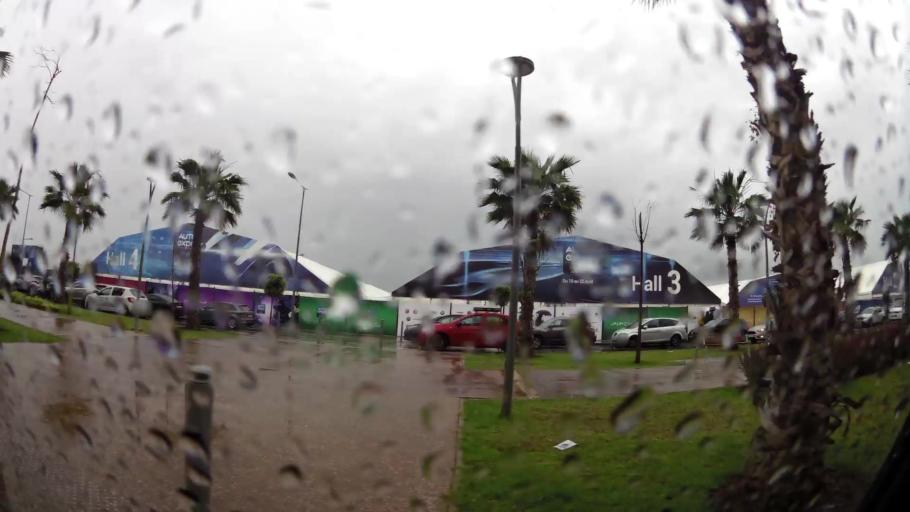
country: MA
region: Grand Casablanca
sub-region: Casablanca
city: Casablanca
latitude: 33.5511
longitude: -7.6661
